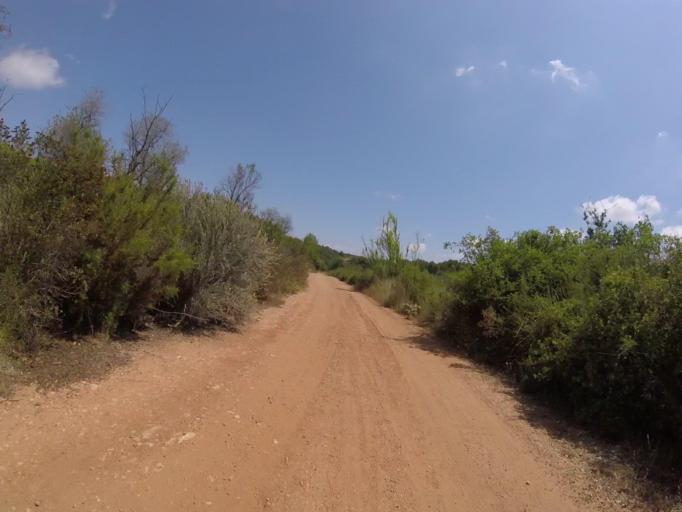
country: ES
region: Valencia
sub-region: Provincia de Castello
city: Torreblanca
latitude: 40.2133
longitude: 0.1459
